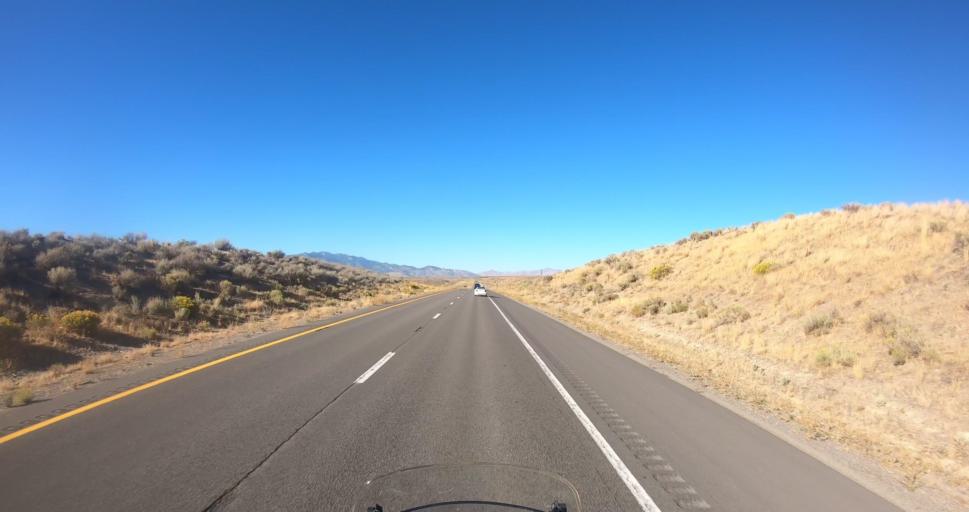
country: US
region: Nevada
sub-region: Washoe County
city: Cold Springs
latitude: 39.7603
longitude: -120.0387
